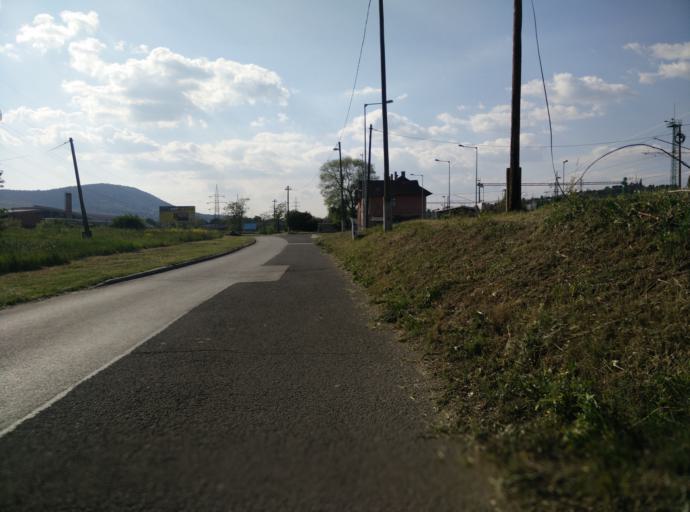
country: HU
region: Budapest
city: Budapest III. keruelet
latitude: 47.5686
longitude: 19.0332
